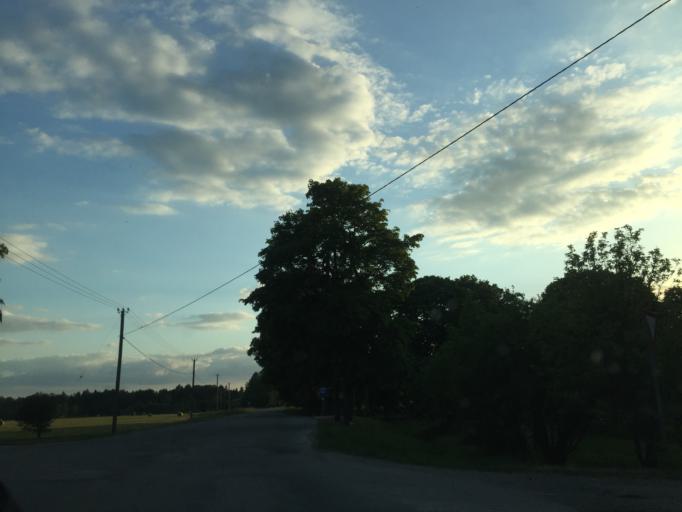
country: LV
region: Sigulda
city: Sigulda
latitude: 57.1090
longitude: 24.9348
